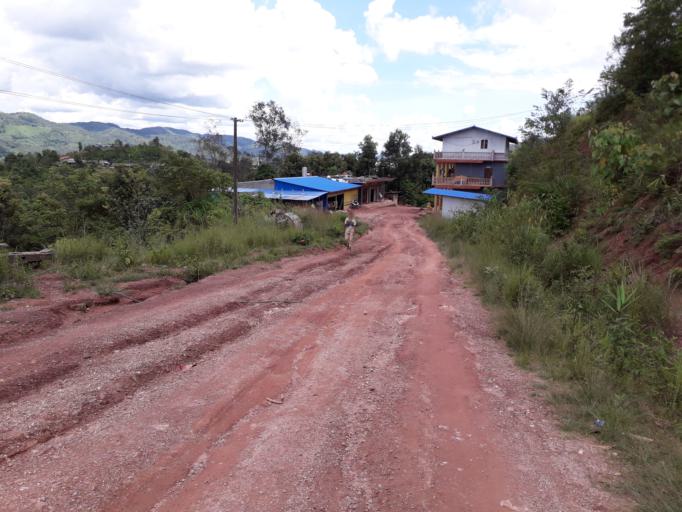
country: CN
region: Yunnan
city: Menglie
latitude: 22.2665
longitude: 101.5725
